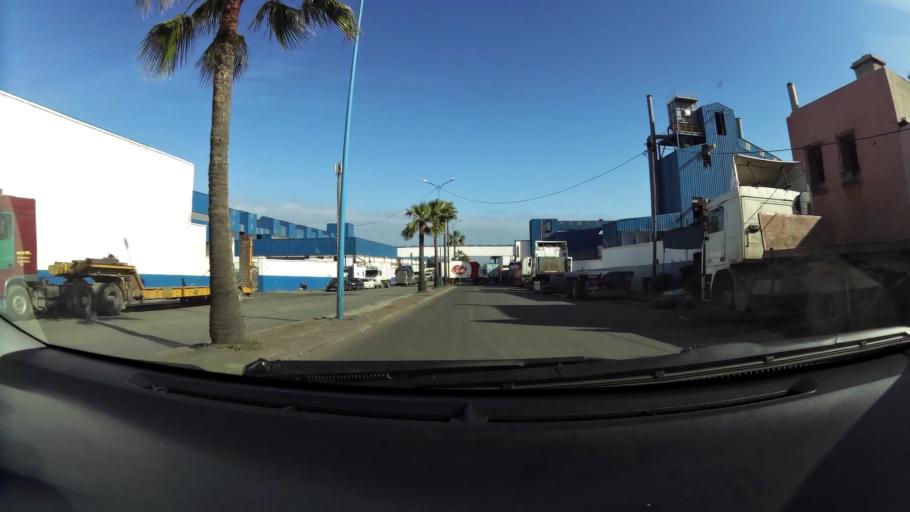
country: MA
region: Grand Casablanca
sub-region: Casablanca
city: Casablanca
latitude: 33.6015
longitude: -7.5734
